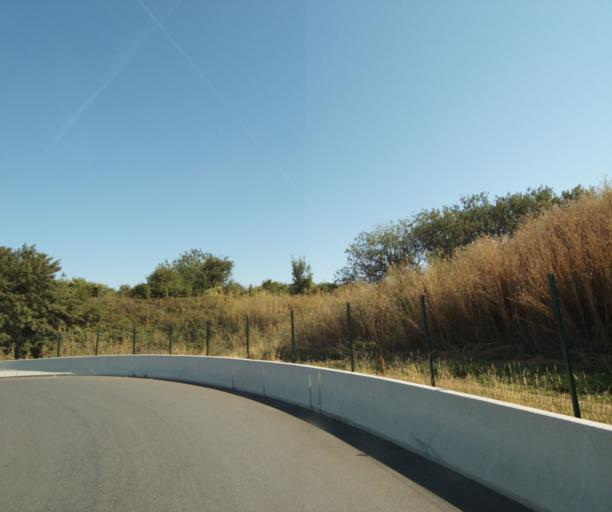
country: FR
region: Ile-de-France
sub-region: Departement de Seine-et-Marne
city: Moissy-Cramayel
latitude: 48.6127
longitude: 2.5839
